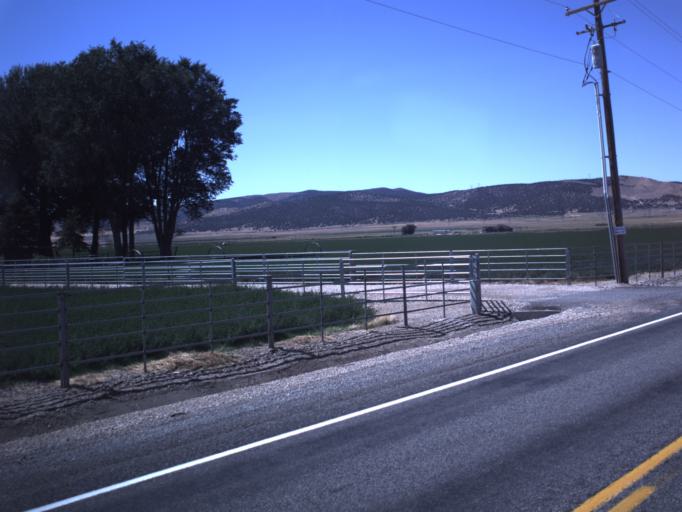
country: US
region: Utah
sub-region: Juab County
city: Nephi
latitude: 39.7101
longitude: -111.8766
